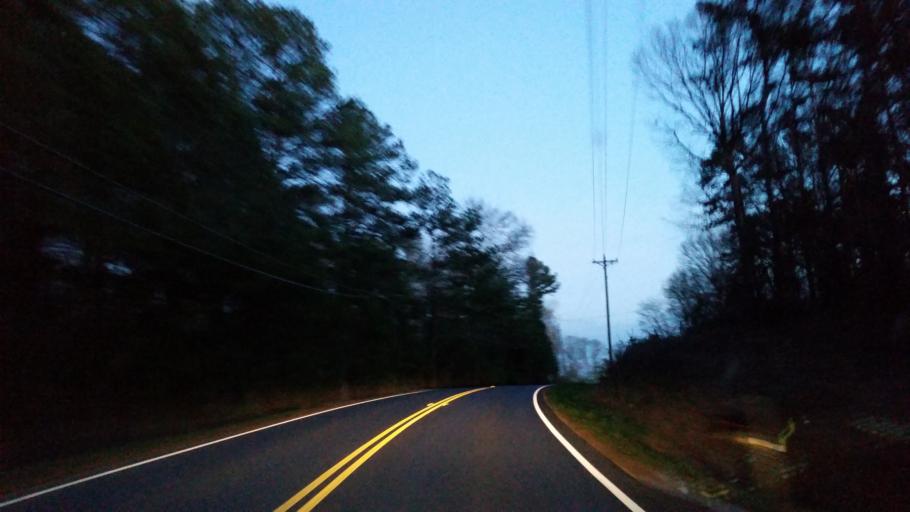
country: US
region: Georgia
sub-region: Cherokee County
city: Ball Ground
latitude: 34.2991
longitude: -84.4440
